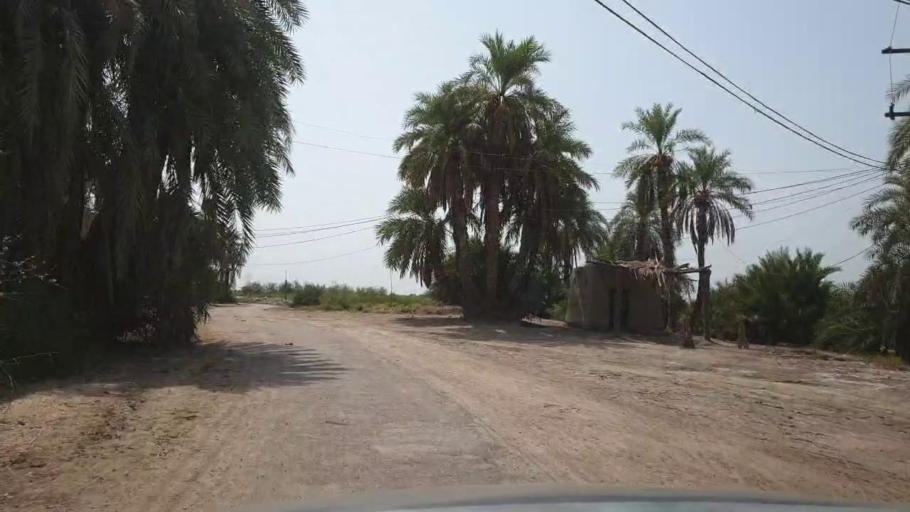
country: PK
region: Sindh
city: Garhi Yasin
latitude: 27.8901
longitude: 68.4646
